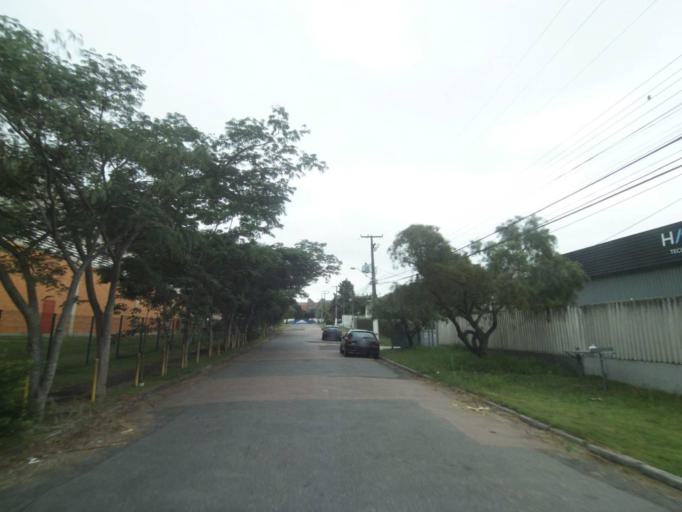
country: BR
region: Parana
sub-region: Sao Jose Dos Pinhais
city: Sao Jose dos Pinhais
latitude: -25.5279
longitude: -49.3167
